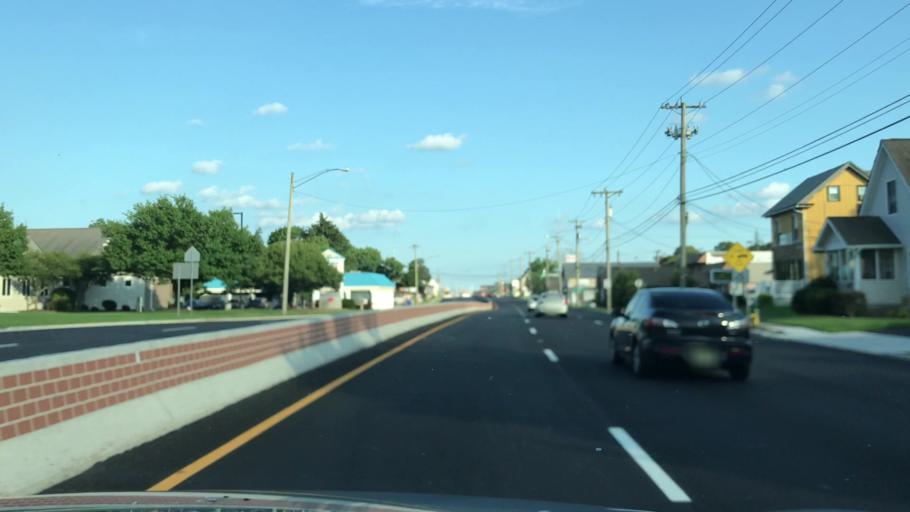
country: US
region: New Jersey
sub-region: Atlantic County
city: Absecon
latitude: 39.4270
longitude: -74.5041
